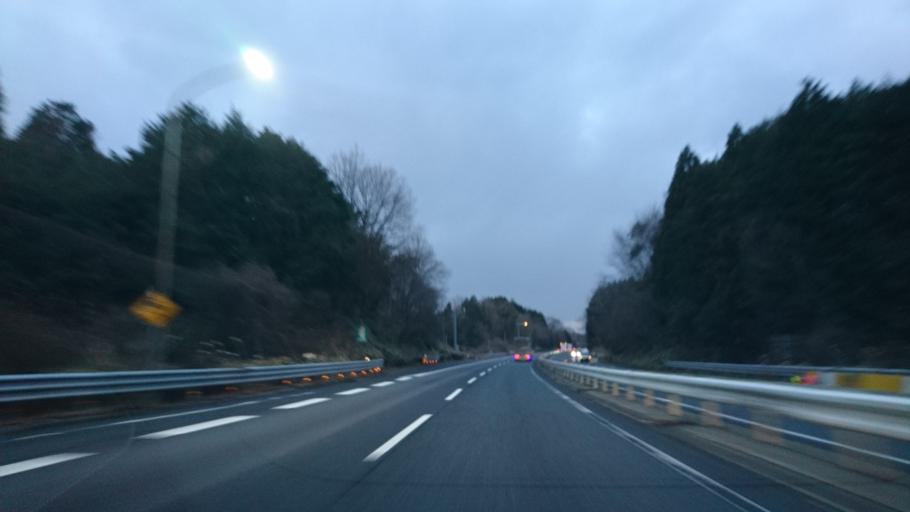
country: JP
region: Mie
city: Nabari
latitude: 34.6383
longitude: 136.0052
